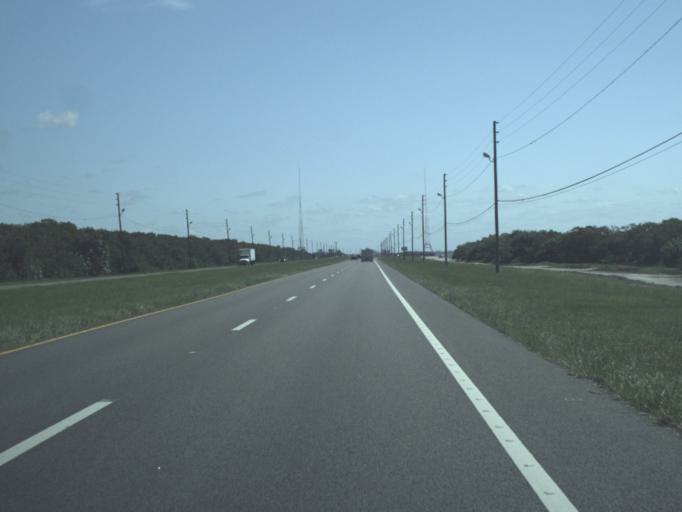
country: US
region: Florida
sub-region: Pinellas County
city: Gandy
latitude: 27.8739
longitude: -82.6022
